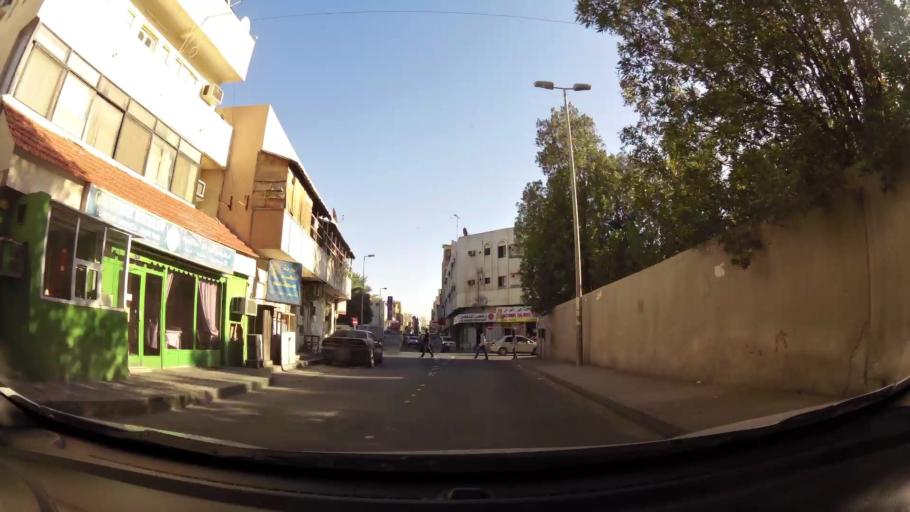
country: BH
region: Manama
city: Manama
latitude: 26.2288
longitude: 50.5854
